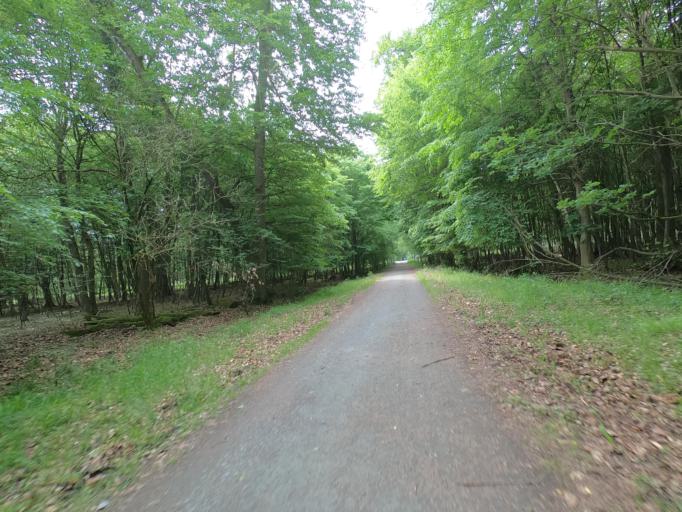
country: DE
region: Hesse
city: Morfelden-Walldorf
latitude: 49.9743
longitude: 8.5418
